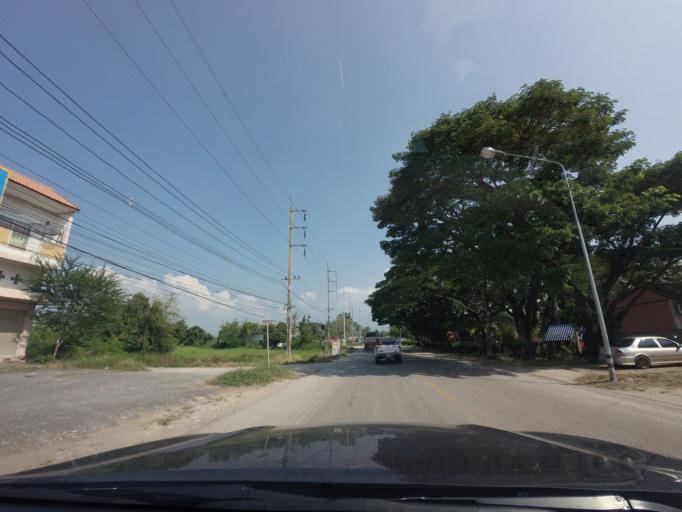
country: TH
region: Phitsanulok
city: Nakhon Thai
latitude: 17.1077
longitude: 100.8291
